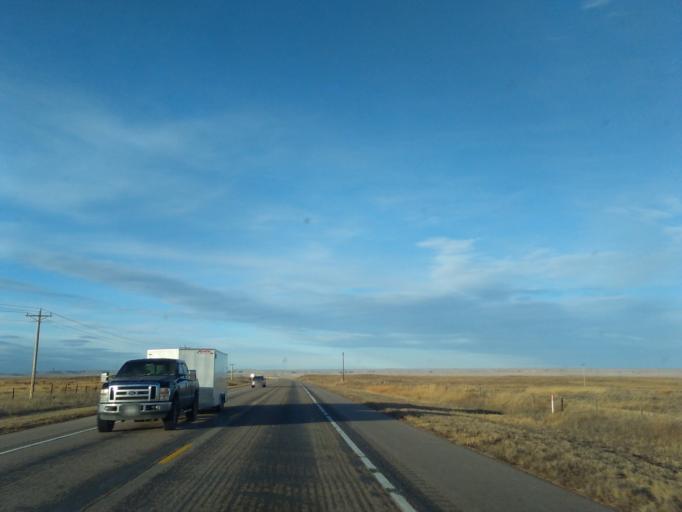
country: US
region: Nebraska
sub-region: Morrill County
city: Bridgeport
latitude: 41.5816
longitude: -102.9841
